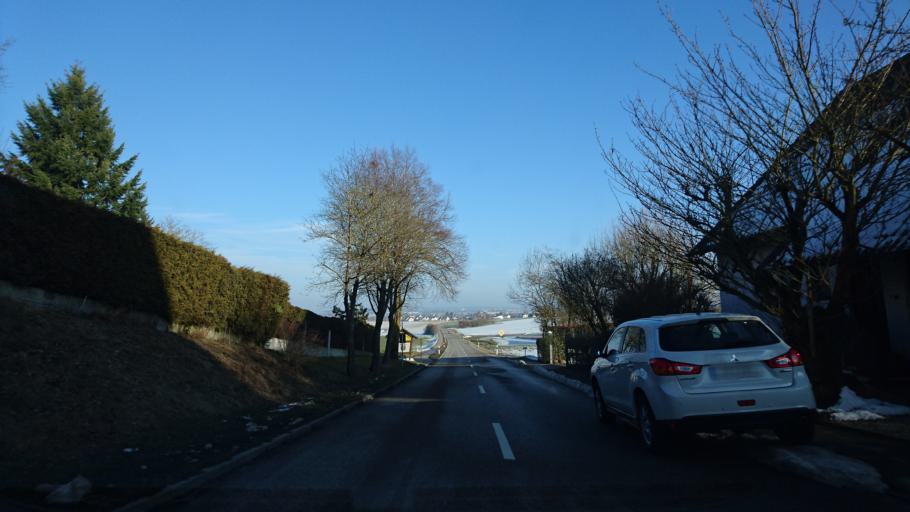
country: DE
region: Bavaria
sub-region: Swabia
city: Gablingen
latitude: 48.4636
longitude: 10.8017
